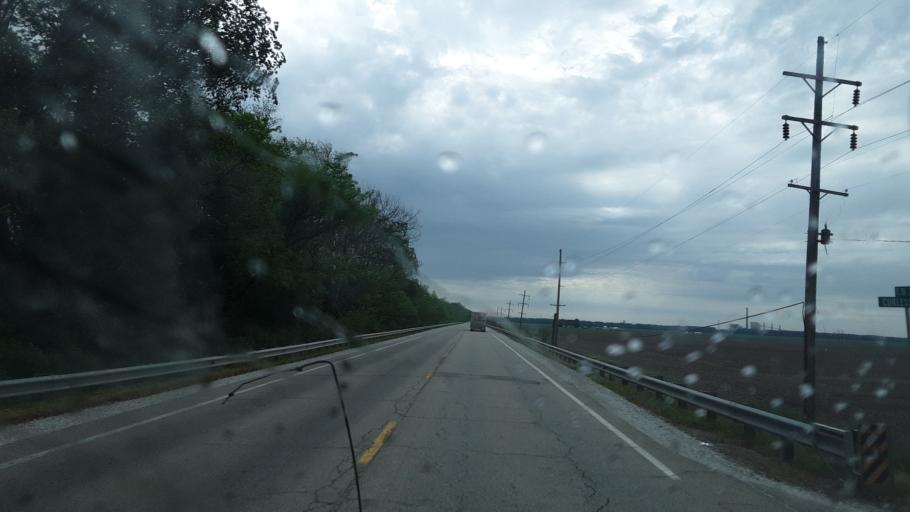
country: US
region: Illinois
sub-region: Mason County
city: Havana
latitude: 40.3028
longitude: -90.1246
